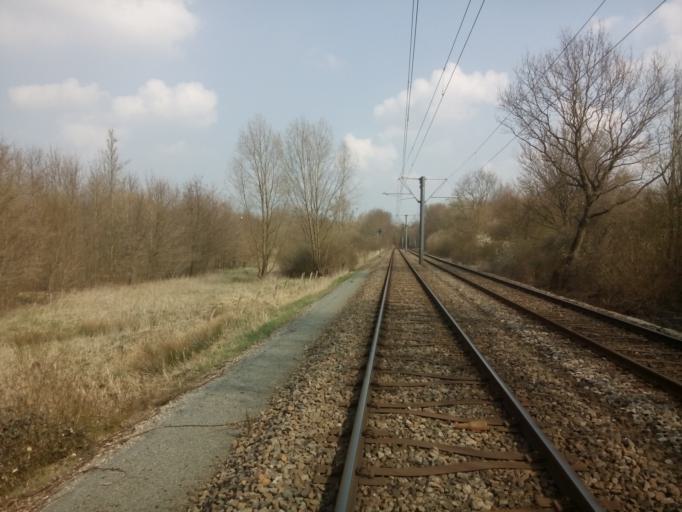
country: DE
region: Lower Saxony
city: Stuhr
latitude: 53.0516
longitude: 8.7474
